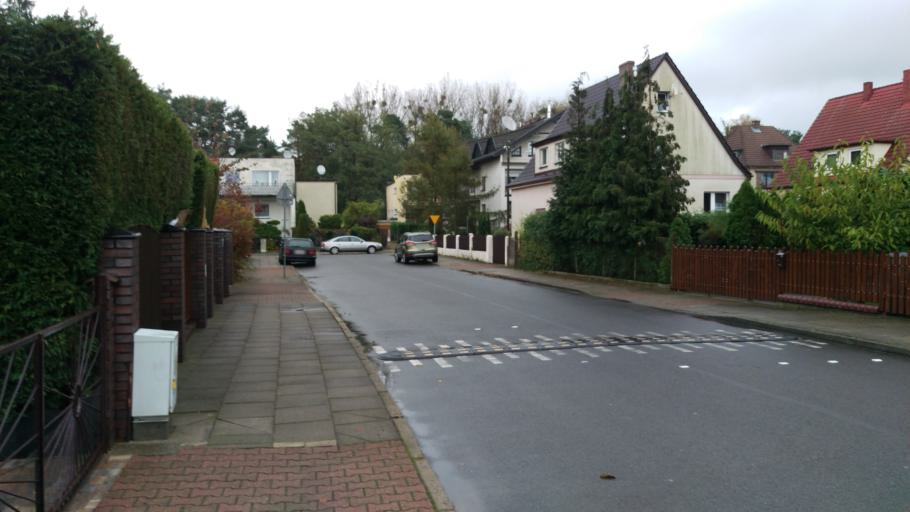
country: PL
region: West Pomeranian Voivodeship
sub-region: Szczecin
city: Szczecin
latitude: 53.4013
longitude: 14.6781
